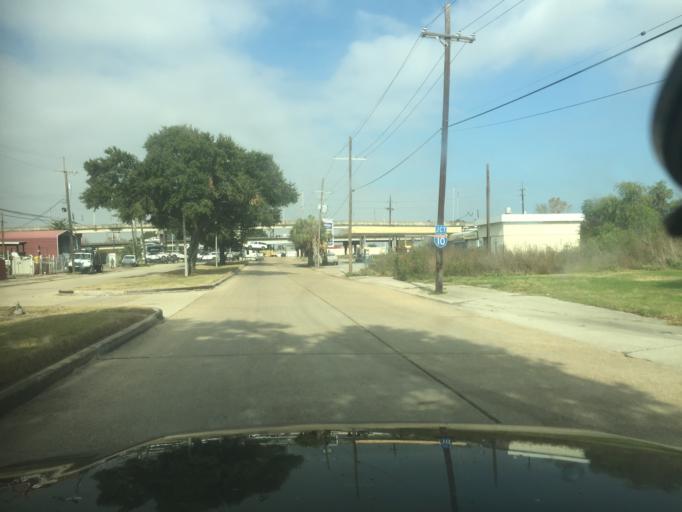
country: US
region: Louisiana
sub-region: Saint Bernard Parish
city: Arabi
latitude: 30.0009
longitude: -90.0352
